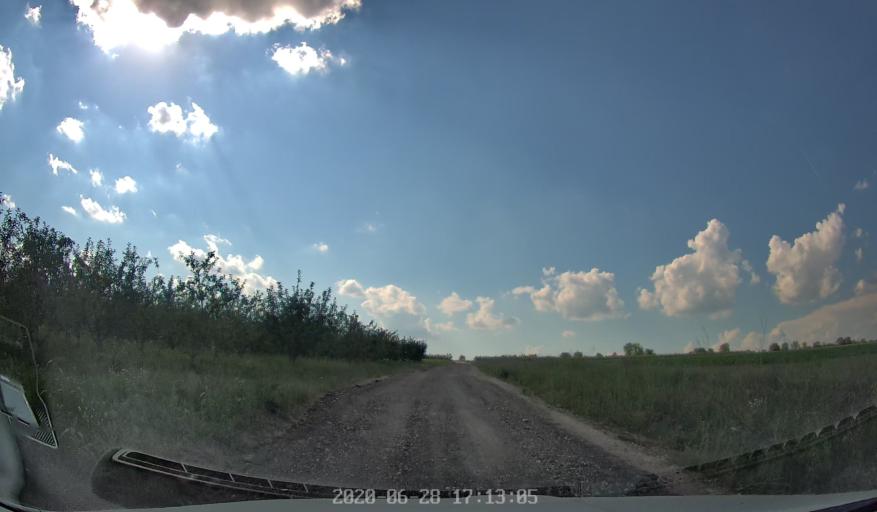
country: MD
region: Chisinau
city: Vatra
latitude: 46.9901
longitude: 28.6983
